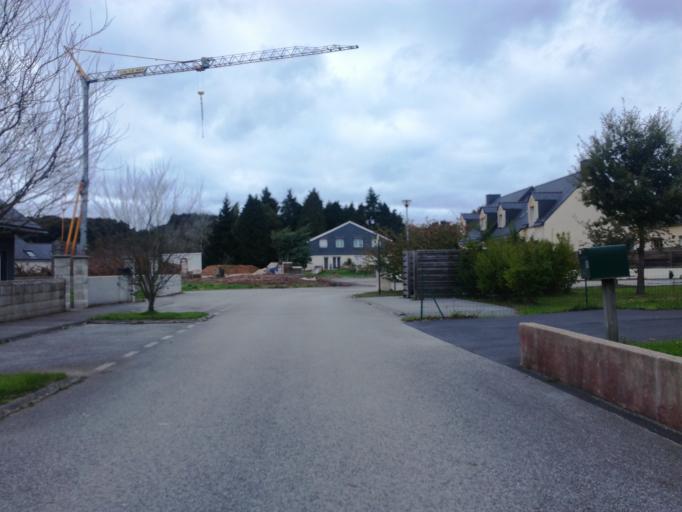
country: FR
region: Brittany
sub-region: Departement du Morbihan
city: Le Sourn
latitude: 48.0402
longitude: -2.9873
